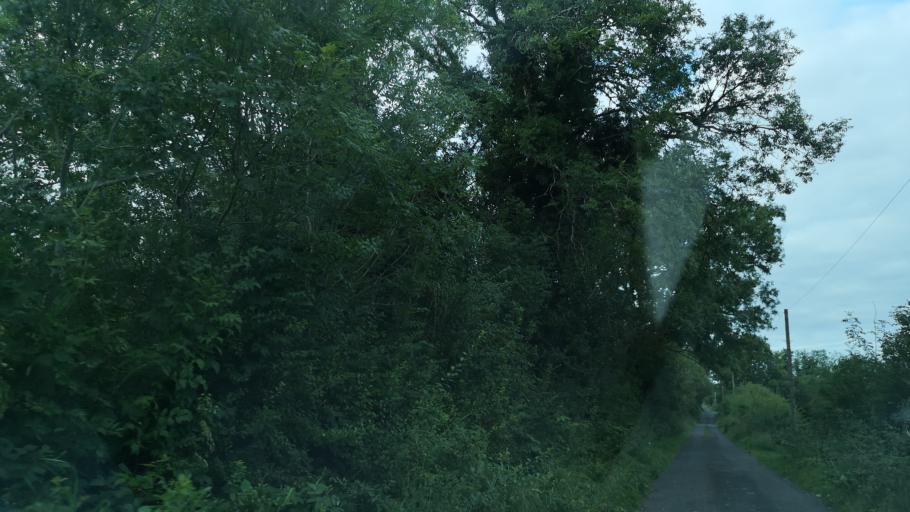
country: IE
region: Connaught
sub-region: County Galway
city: Loughrea
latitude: 53.1458
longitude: -8.5169
